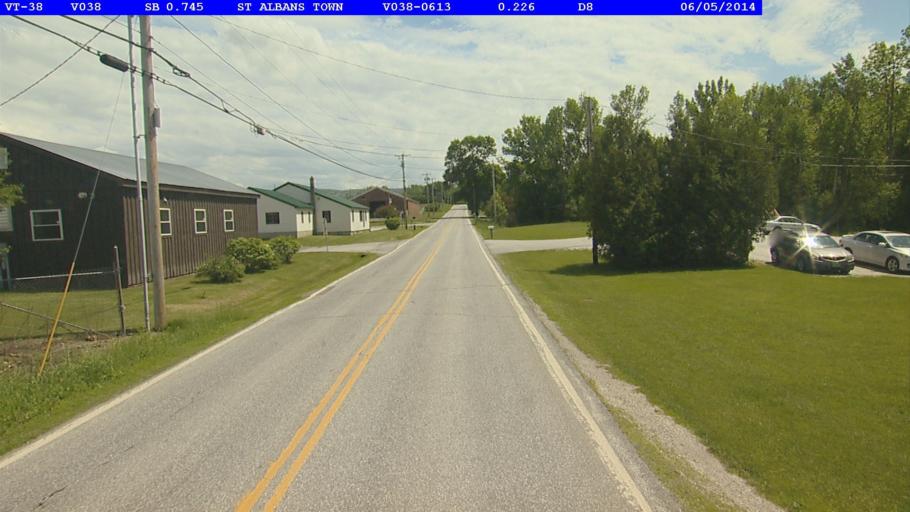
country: US
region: Vermont
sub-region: Franklin County
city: Saint Albans
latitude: 44.8270
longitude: -73.0910
